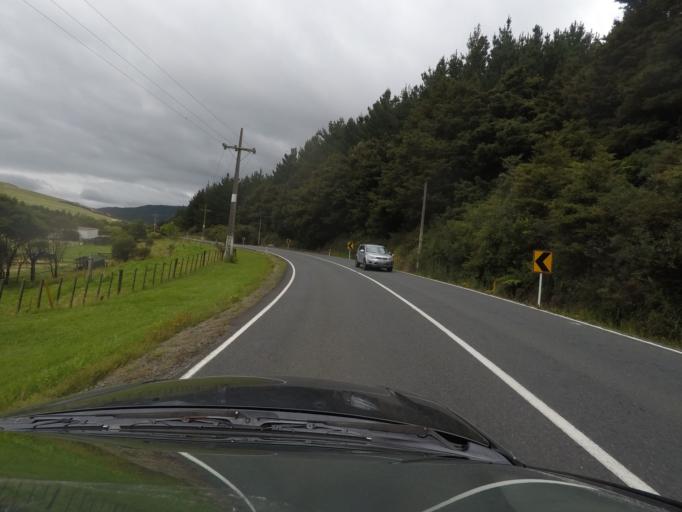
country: NZ
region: Auckland
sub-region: Auckland
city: Wellsford
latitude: -36.2872
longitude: 174.6128
